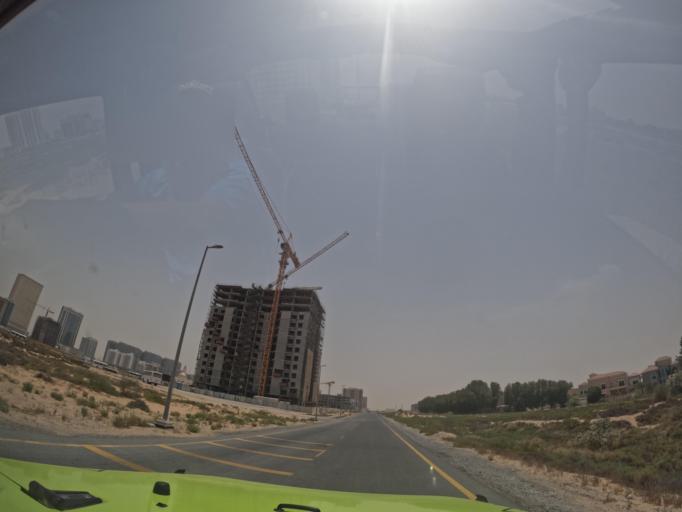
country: AE
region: Dubai
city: Dubai
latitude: 25.0934
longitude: 55.3733
